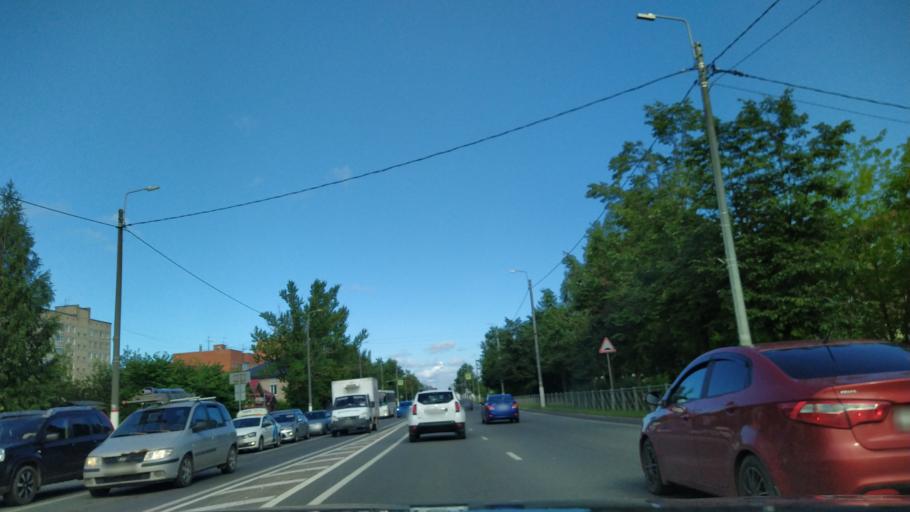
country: RU
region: Leningrad
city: Tosno
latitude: 59.5456
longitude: 30.8687
